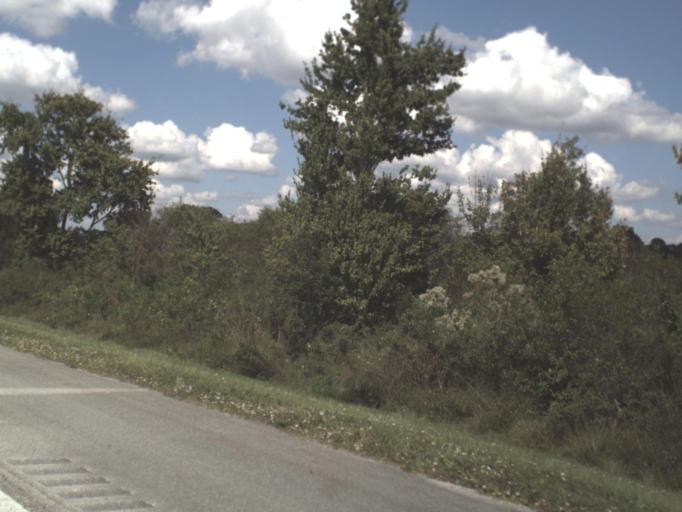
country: US
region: Florida
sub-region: Indian River County
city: Fellsmere
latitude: 27.6033
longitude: -80.8228
